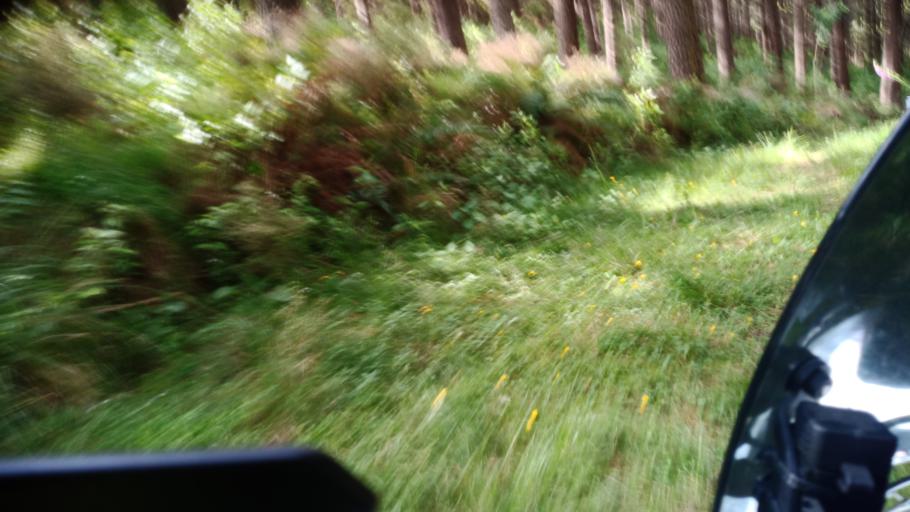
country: NZ
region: Gisborne
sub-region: Gisborne District
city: Gisborne
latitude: -38.4577
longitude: 177.9249
